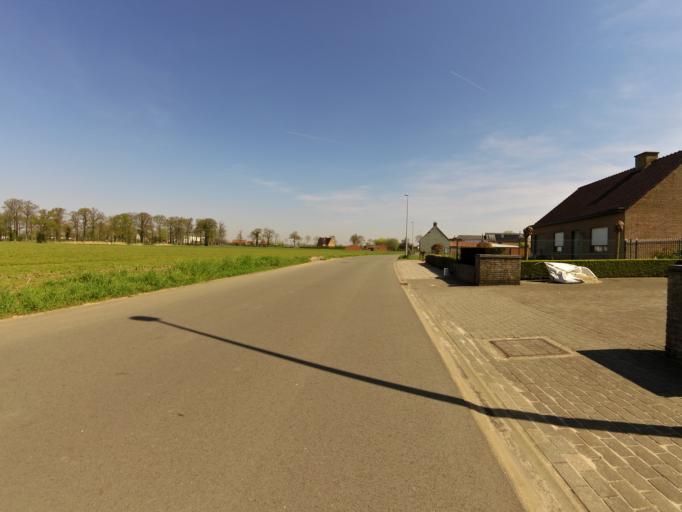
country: BE
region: Flanders
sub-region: Provincie West-Vlaanderen
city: Ichtegem
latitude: 51.1098
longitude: 3.0107
